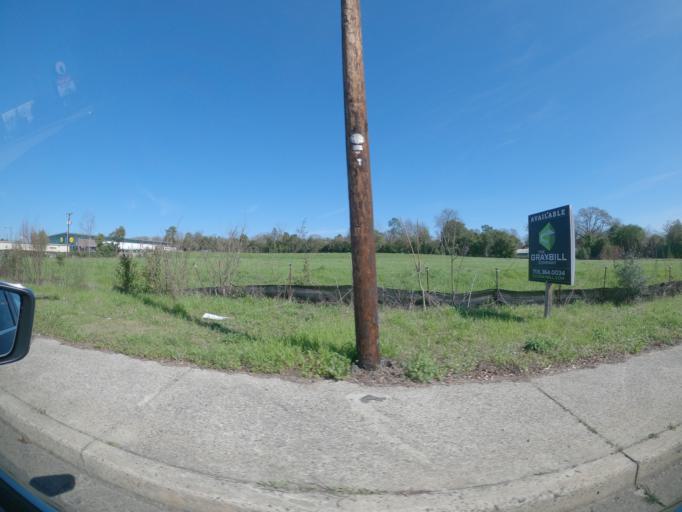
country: US
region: South Carolina
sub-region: Aiken County
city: North Augusta
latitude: 33.4952
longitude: -81.9577
